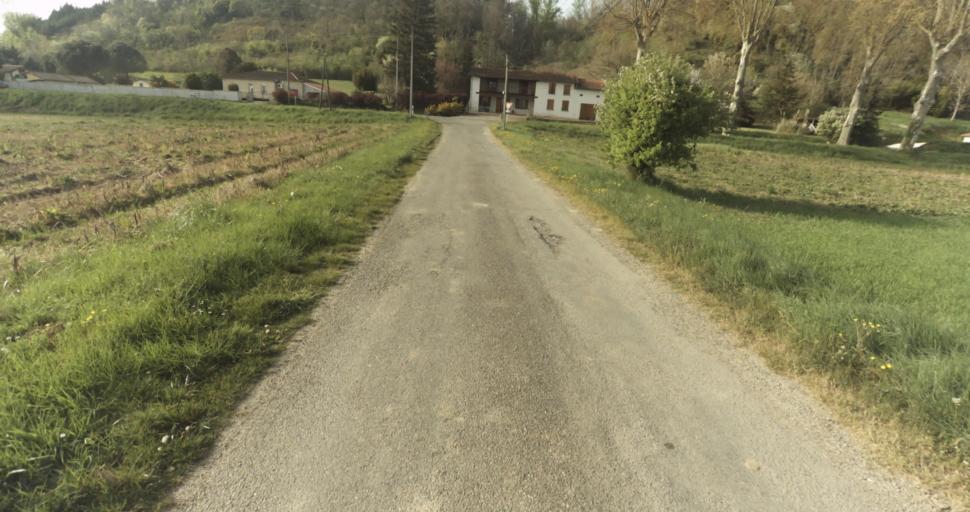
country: FR
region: Midi-Pyrenees
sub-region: Departement du Tarn-et-Garonne
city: Moissac
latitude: 44.1206
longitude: 1.1267
